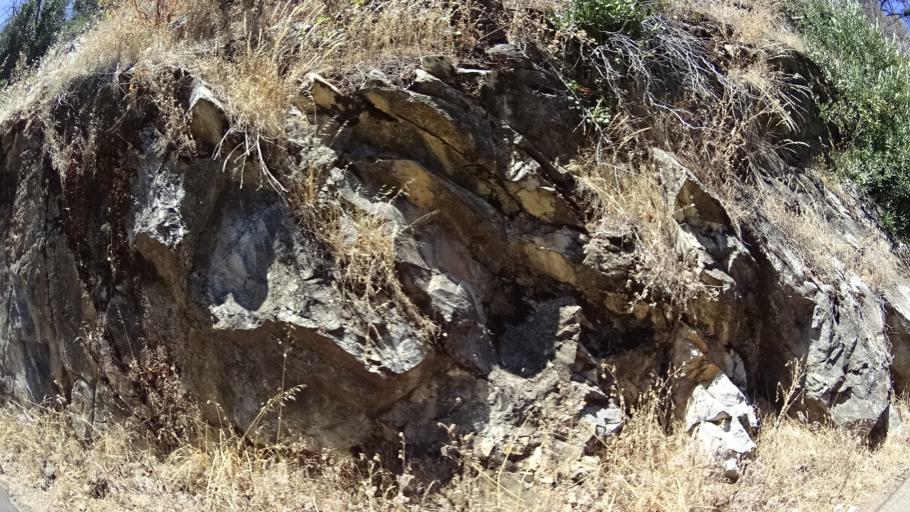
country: US
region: California
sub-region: Calaveras County
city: San Andreas
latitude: 38.2870
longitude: -120.6640
